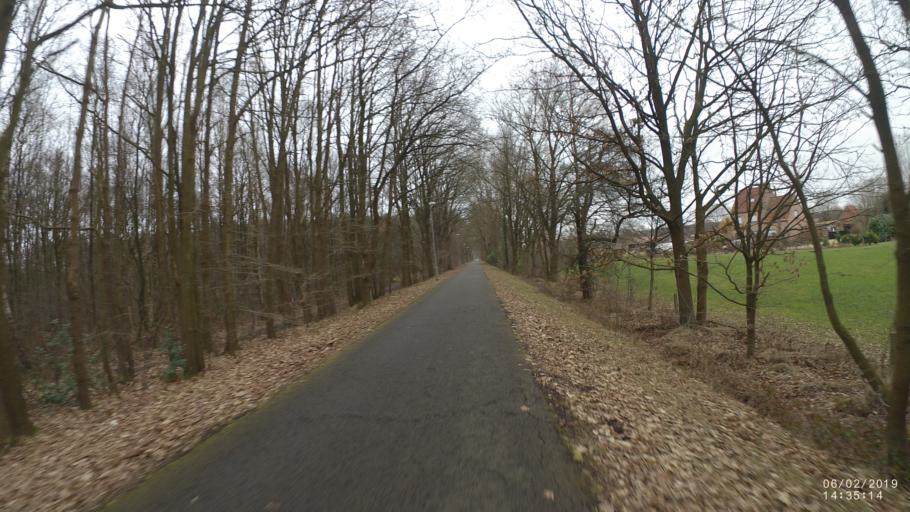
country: BE
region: Flanders
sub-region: Provincie Vlaams-Brabant
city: Aarschot
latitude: 51.0233
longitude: 4.8285
